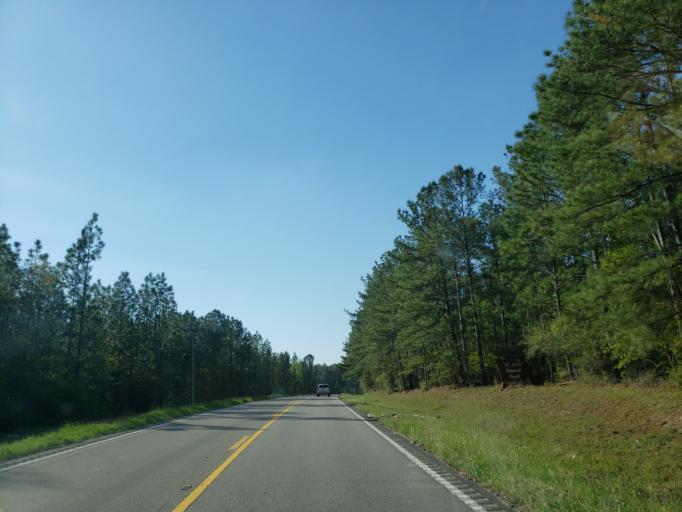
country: US
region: Mississippi
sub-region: Perry County
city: Richton
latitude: 31.4483
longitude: -88.9756
